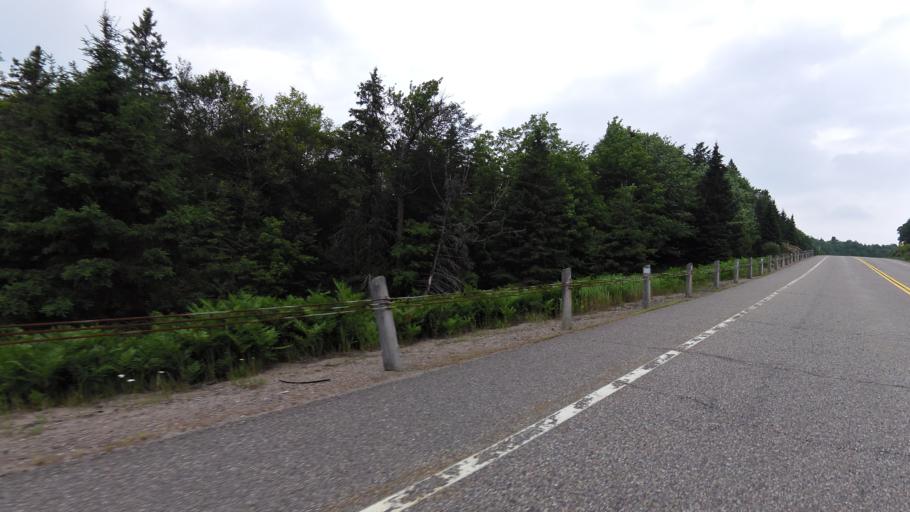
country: CA
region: Ontario
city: Huntsville
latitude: 45.5648
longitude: -78.5660
